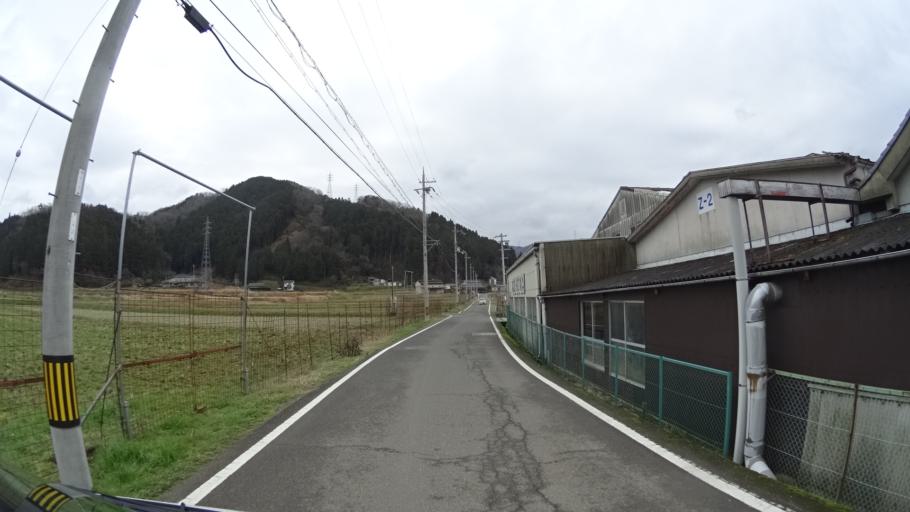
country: JP
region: Kyoto
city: Ayabe
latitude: 35.3346
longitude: 135.3482
